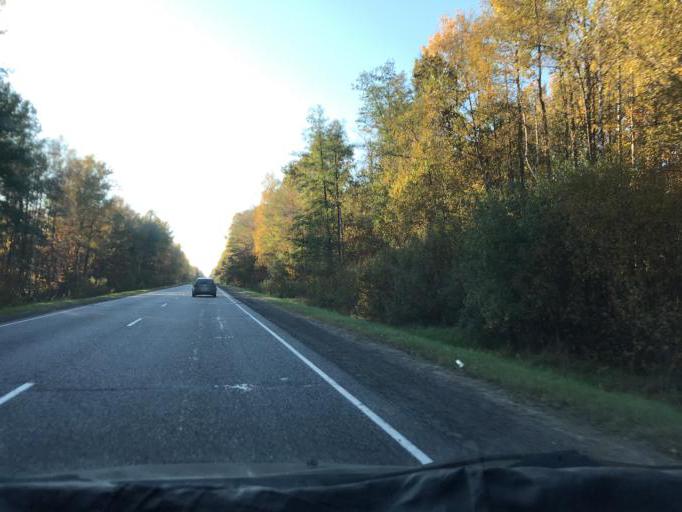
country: BY
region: Gomel
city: Zhytkavichy
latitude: 52.2744
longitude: 28.1586
